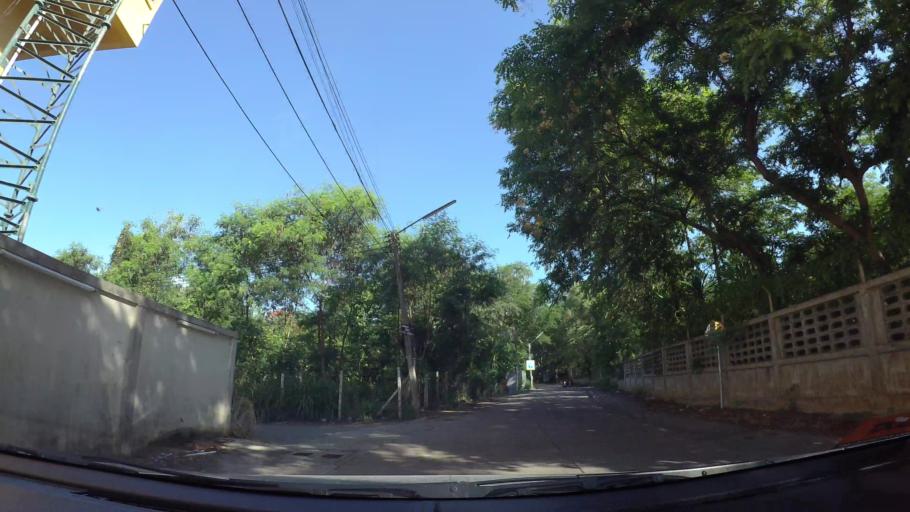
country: TH
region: Chon Buri
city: Si Racha
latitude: 13.1537
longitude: 100.9308
